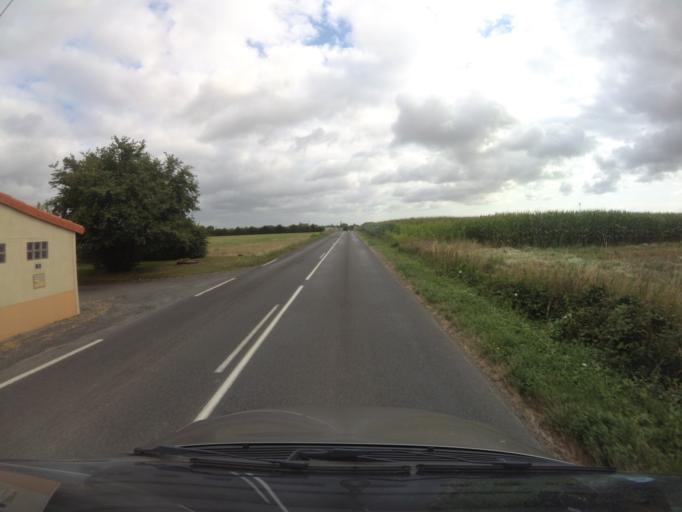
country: FR
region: Pays de la Loire
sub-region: Departement de Maine-et-Loire
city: Villedieu-la-Blouere
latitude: 47.1377
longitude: -1.0751
